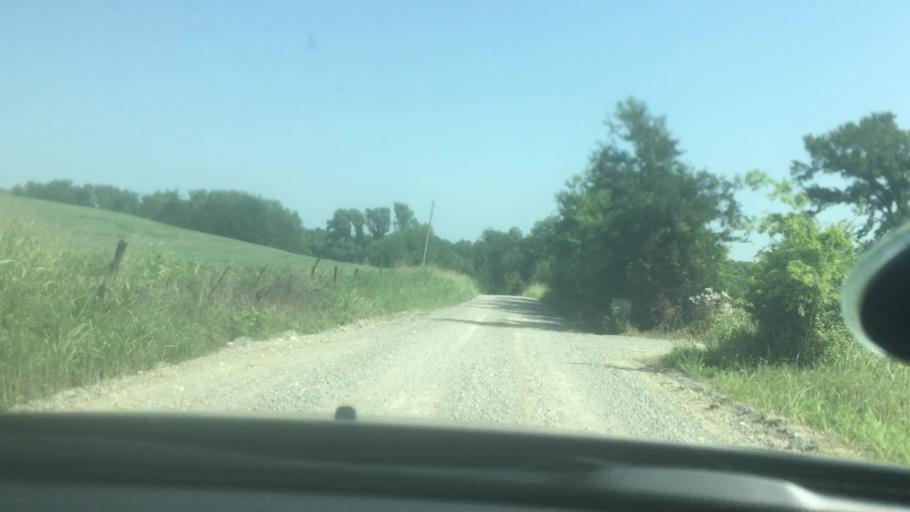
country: US
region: Oklahoma
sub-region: Bryan County
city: Durant
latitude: 34.0966
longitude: -96.4077
